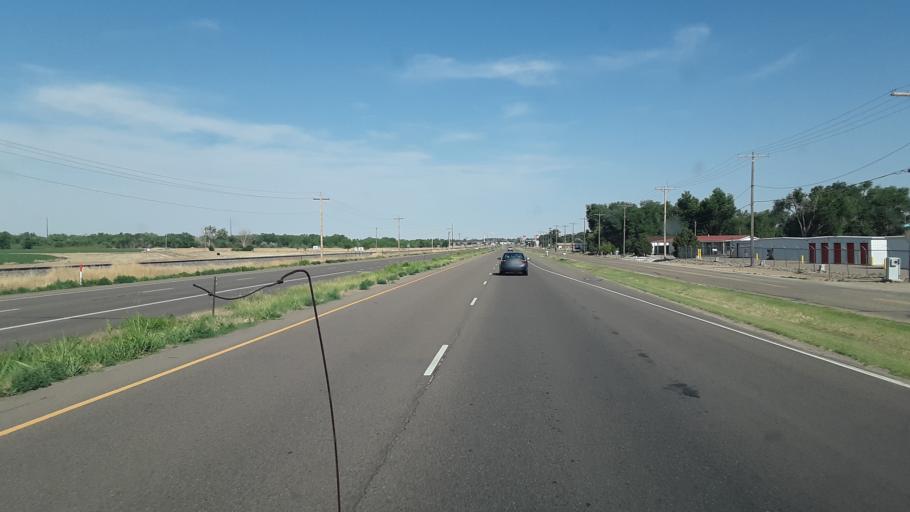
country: US
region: Colorado
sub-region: Otero County
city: La Junta
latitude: 37.9964
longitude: -103.5818
